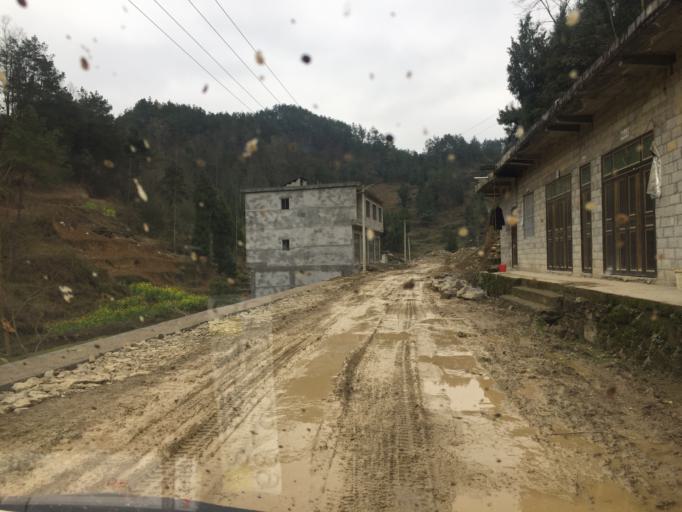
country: CN
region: Guizhou Sheng
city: Fuxing
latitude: 28.0432
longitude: 107.9138
